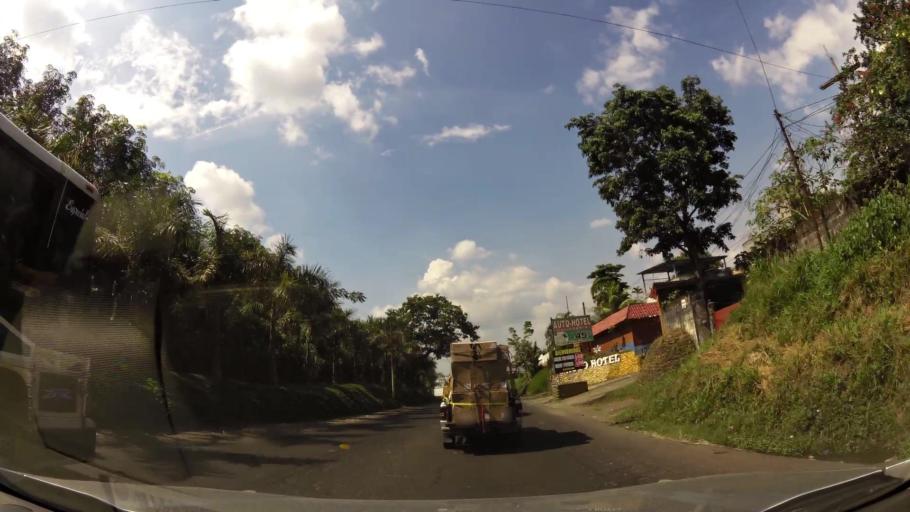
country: GT
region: Suchitepeque
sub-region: Municipio de Cuyotenango
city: Cuyotenango
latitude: 14.5425
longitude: -91.5446
